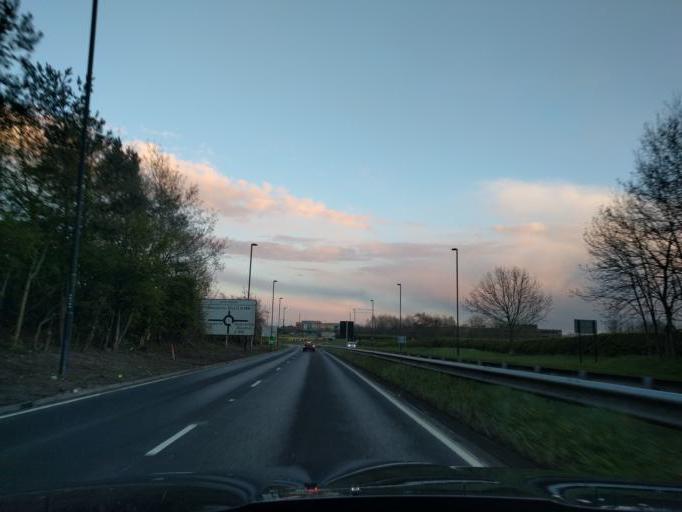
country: GB
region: England
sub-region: Newcastle upon Tyne
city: Gosforth
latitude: 55.0276
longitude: -1.5883
